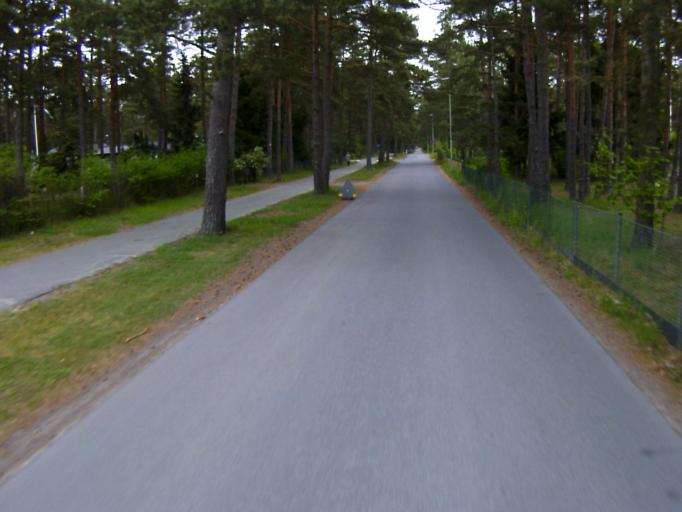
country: SE
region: Skane
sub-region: Kristianstads Kommun
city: Ahus
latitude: 55.9419
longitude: 14.3186
